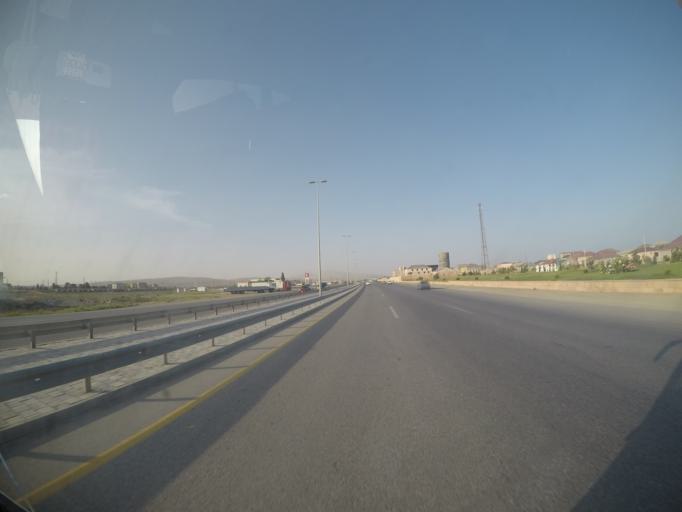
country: AZ
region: Baki
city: Korgoz
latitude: 40.2213
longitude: 49.5635
